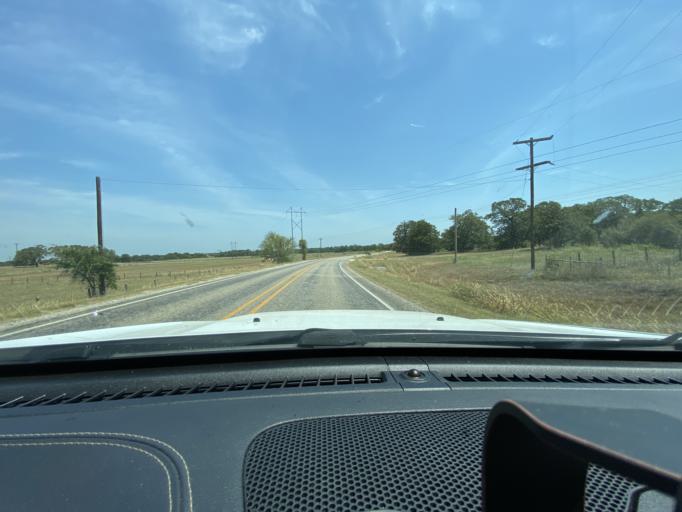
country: US
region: Texas
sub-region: Lee County
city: Giddings
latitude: 30.1419
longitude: -96.9628
